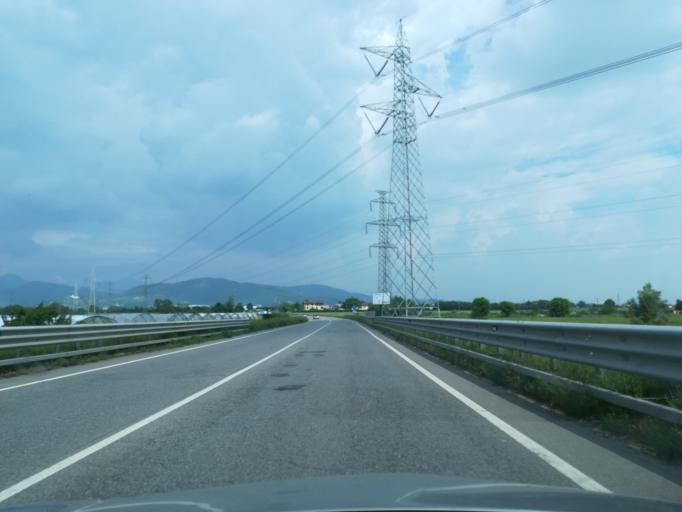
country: IT
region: Lombardy
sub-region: Provincia di Bergamo
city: Costa di Mezzate
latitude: 45.6551
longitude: 9.7904
